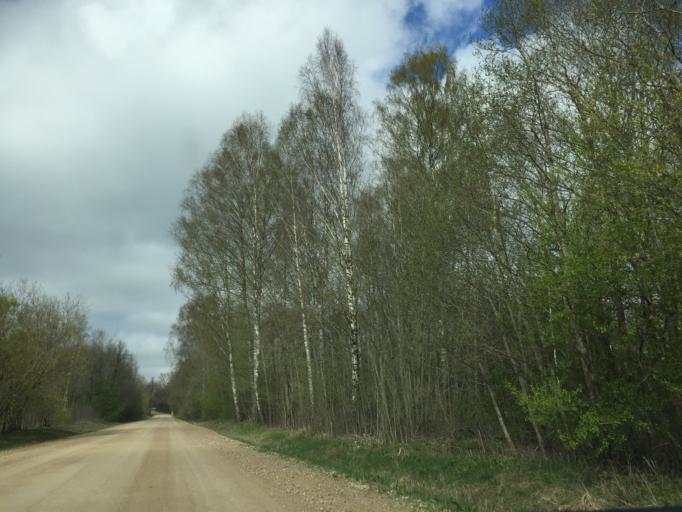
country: LV
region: Apes Novads
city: Ape
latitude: 57.5298
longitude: 26.3680
